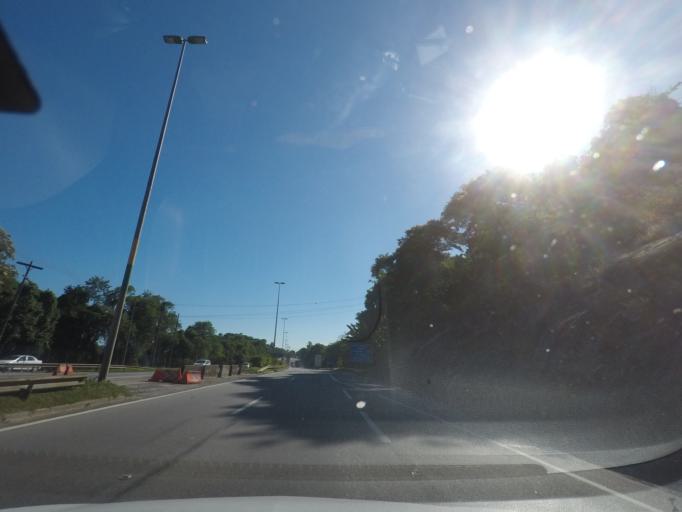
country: BR
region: Rio de Janeiro
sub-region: Guapimirim
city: Guapimirim
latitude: -22.6593
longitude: -43.0912
